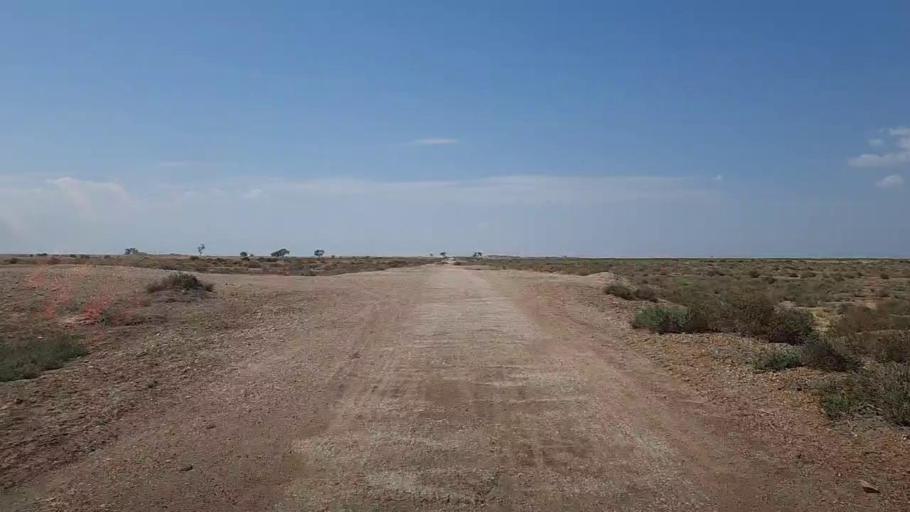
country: PK
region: Sindh
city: Sehwan
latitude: 26.3555
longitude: 67.6709
